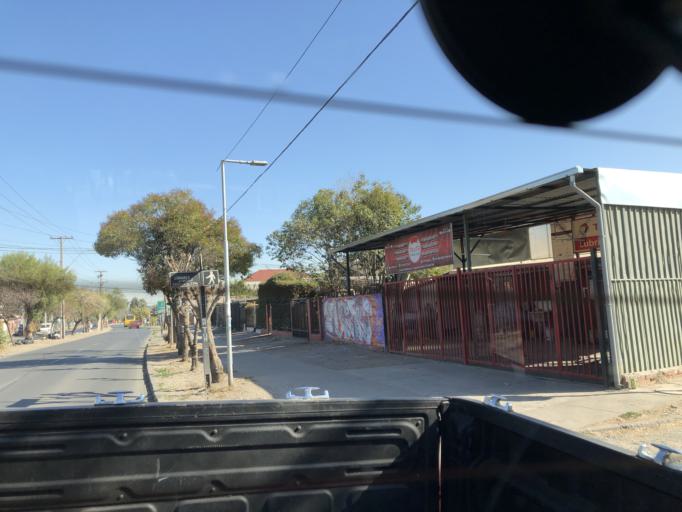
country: CL
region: Santiago Metropolitan
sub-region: Provincia de Cordillera
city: Puente Alto
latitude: -33.5765
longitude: -70.5714
